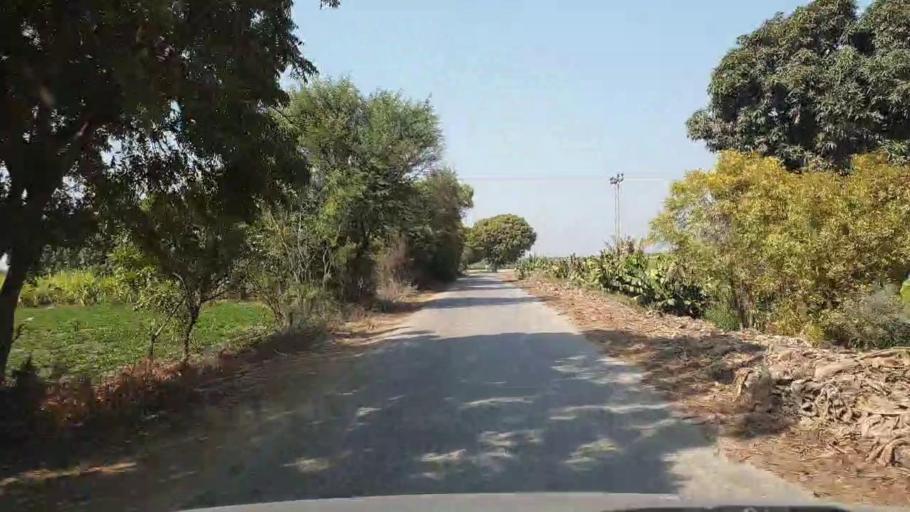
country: PK
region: Sindh
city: Tando Allahyar
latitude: 25.4361
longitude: 68.6532
